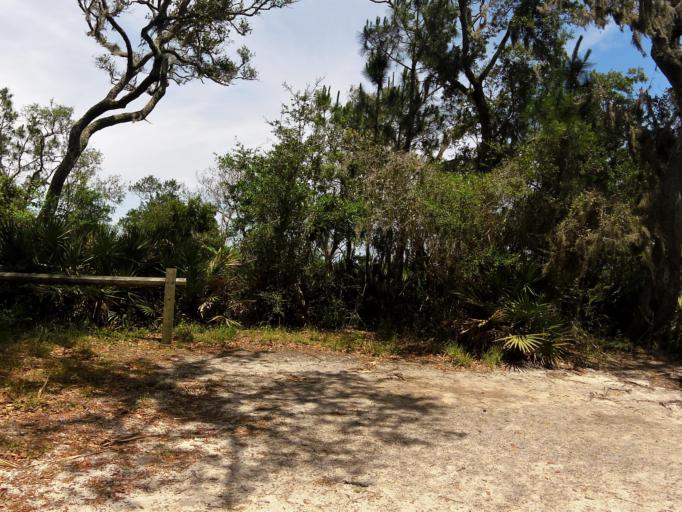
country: US
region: Florida
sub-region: Duval County
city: Atlantic Beach
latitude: 30.4889
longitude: -81.4892
